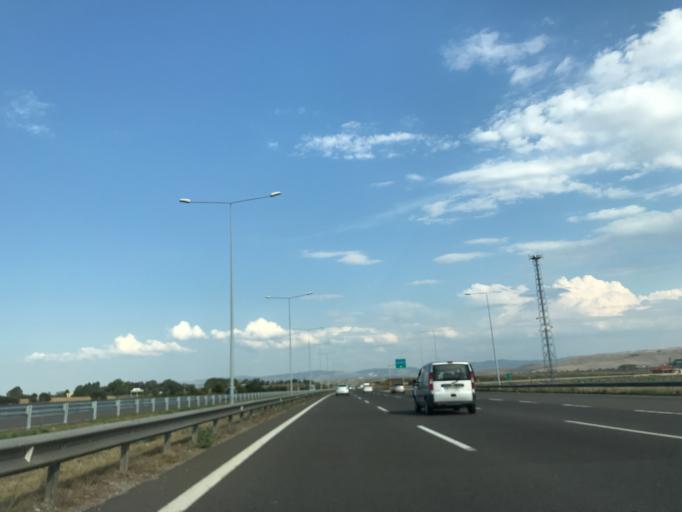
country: TR
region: Bolu
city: Dortdivan
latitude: 40.7451
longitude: 32.1125
